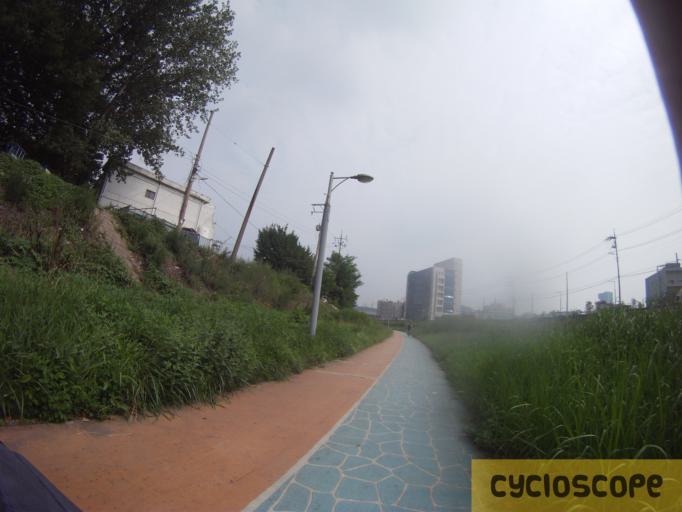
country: KR
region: Gyeonggi-do
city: Anyang-si
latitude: 37.3586
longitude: 126.9575
